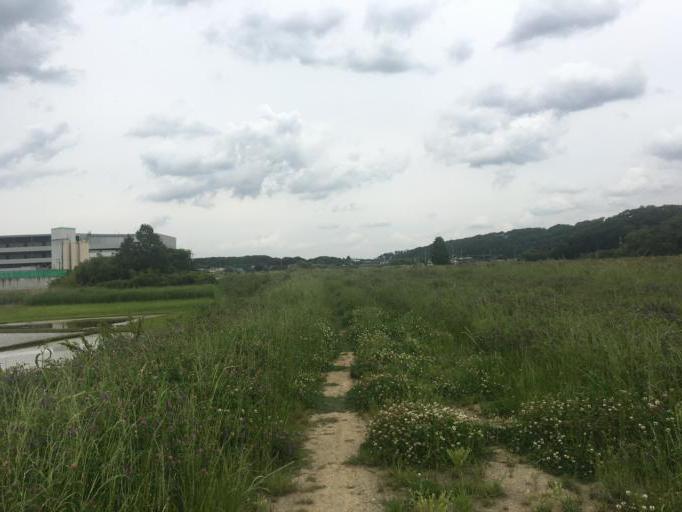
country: JP
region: Saitama
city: Fukiage-fujimi
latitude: 36.0405
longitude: 139.4186
